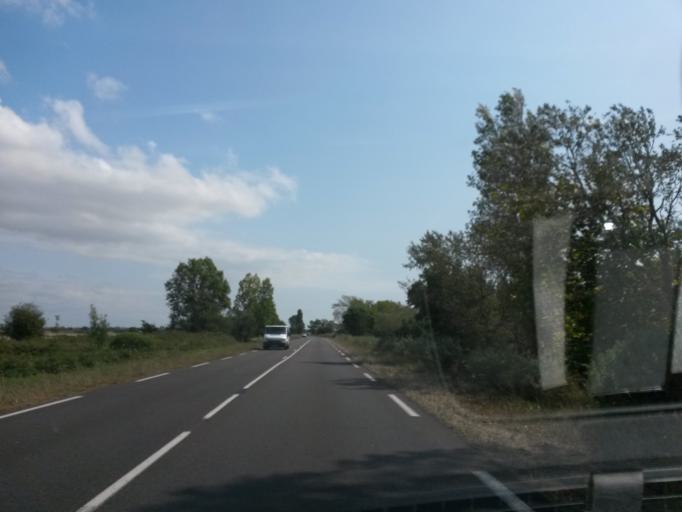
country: FR
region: Pays de la Loire
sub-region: Departement de la Vendee
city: La Tranche-sur-Mer
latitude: 46.3589
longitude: -1.4463
